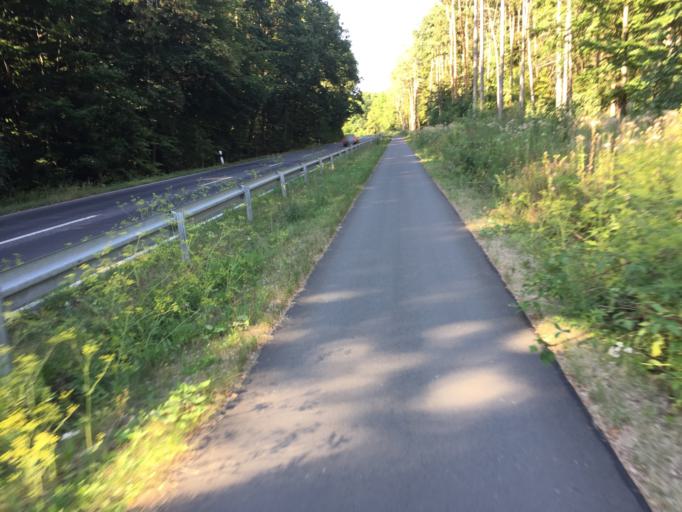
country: DE
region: Hesse
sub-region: Regierungsbezirk Giessen
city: Giessen
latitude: 50.5530
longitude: 8.6809
